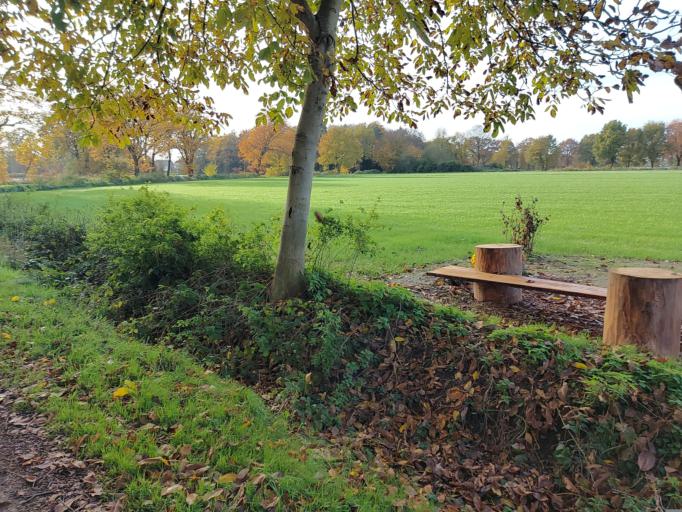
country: BE
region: Flanders
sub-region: Provincie Antwerpen
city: Geel
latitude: 51.1547
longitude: 4.9689
